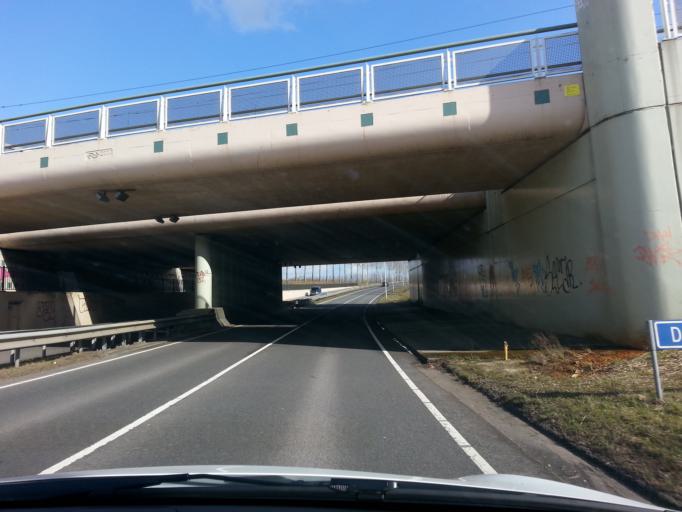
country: NL
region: North Brabant
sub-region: Gemeente Best
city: Best
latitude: 51.5169
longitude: 5.3824
